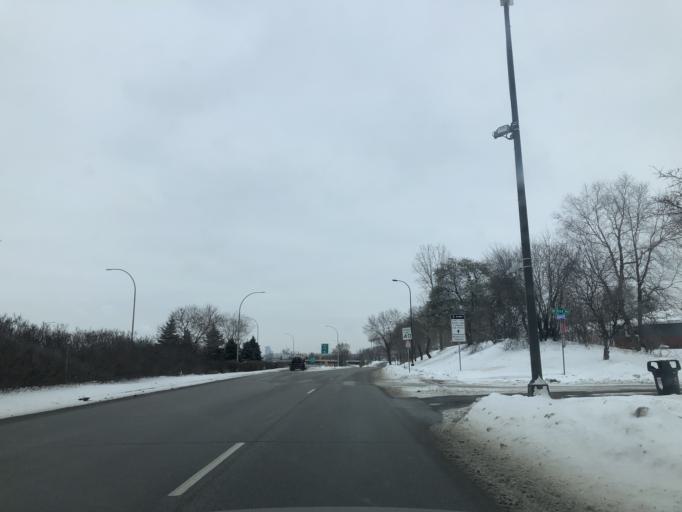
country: US
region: Minnesota
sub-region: Anoka County
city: Columbia Heights
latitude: 45.0478
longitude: -93.2851
